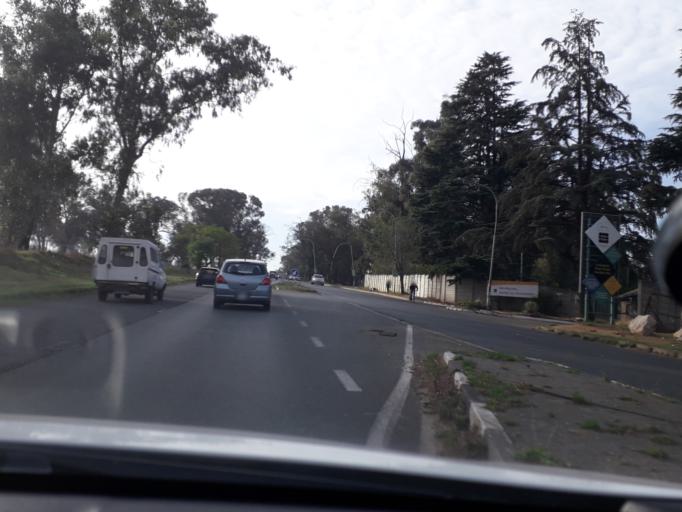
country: ZA
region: Gauteng
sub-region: City of Johannesburg Metropolitan Municipality
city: Modderfontein
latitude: -26.1408
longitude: 28.1198
